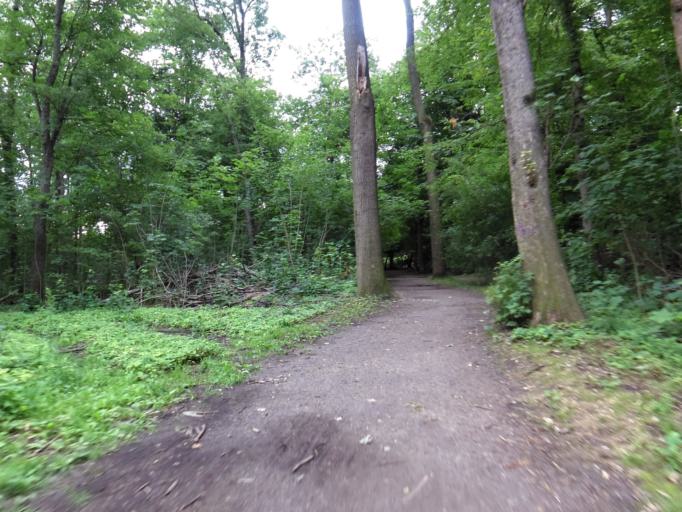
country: DE
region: Saxony
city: Leipzig
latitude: 51.3253
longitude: 12.4214
